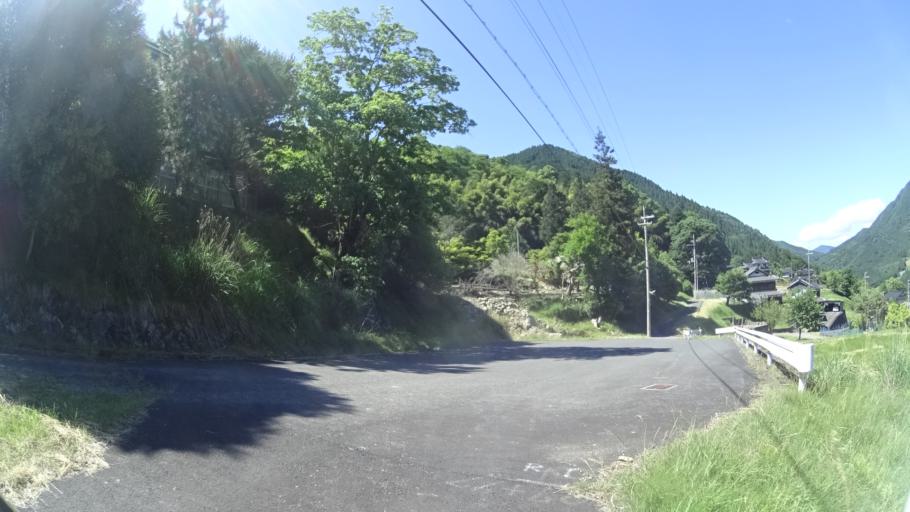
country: JP
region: Kyoto
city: Fukuchiyama
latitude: 35.3809
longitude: 135.0340
